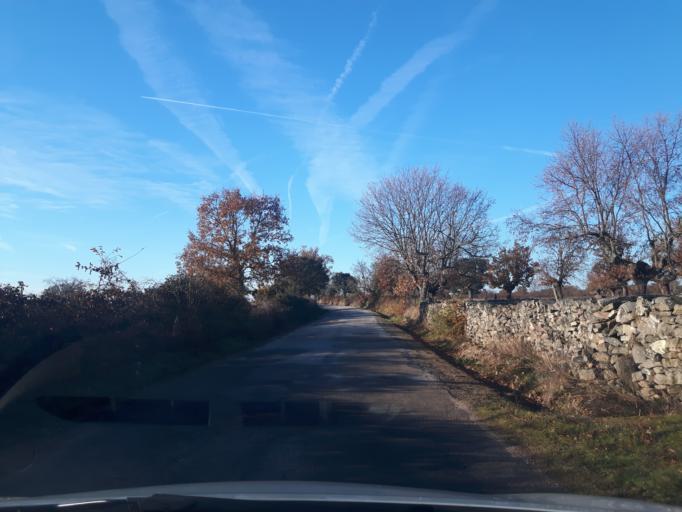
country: ES
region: Castille and Leon
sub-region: Provincia de Salamanca
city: Cerralbo
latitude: 40.9570
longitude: -6.5989
